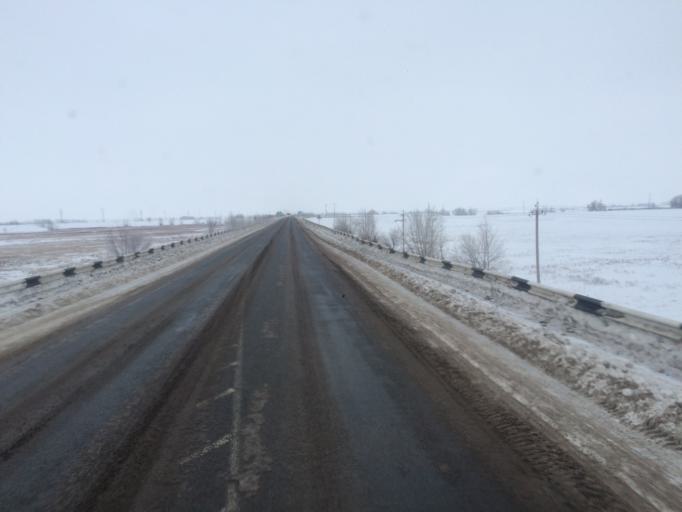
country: KZ
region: Batys Qazaqstan
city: Krugloozernoe
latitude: 51.1233
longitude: 51.3756
